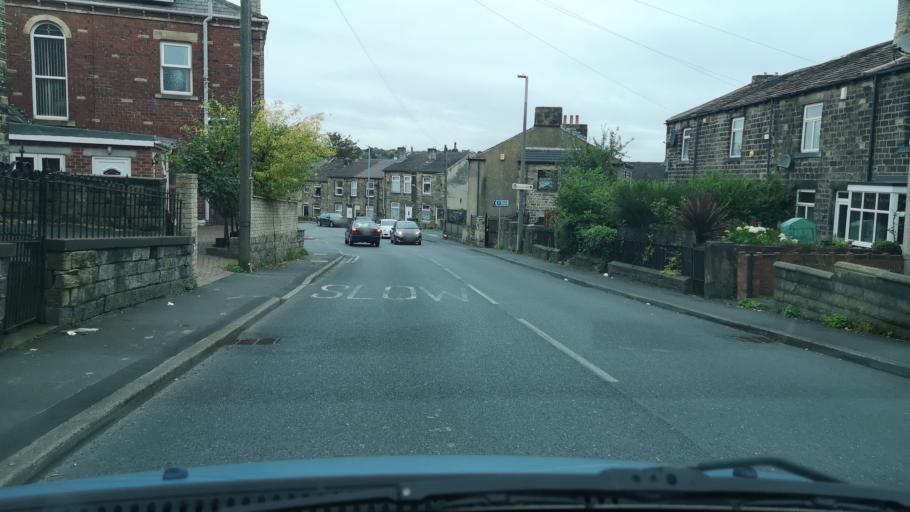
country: GB
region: England
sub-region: Kirklees
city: Heckmondwike
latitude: 53.7100
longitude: -1.6762
